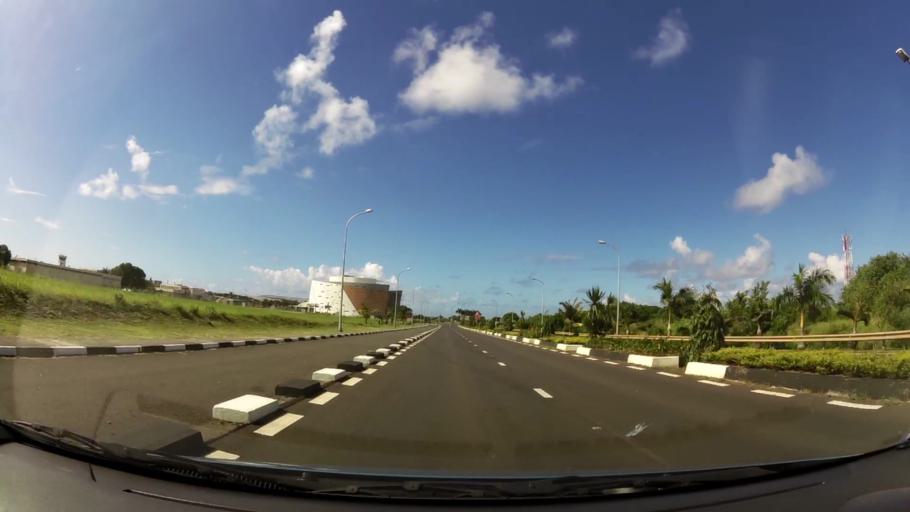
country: MU
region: Grand Port
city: Plaine Magnien
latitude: -20.4332
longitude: 57.6715
